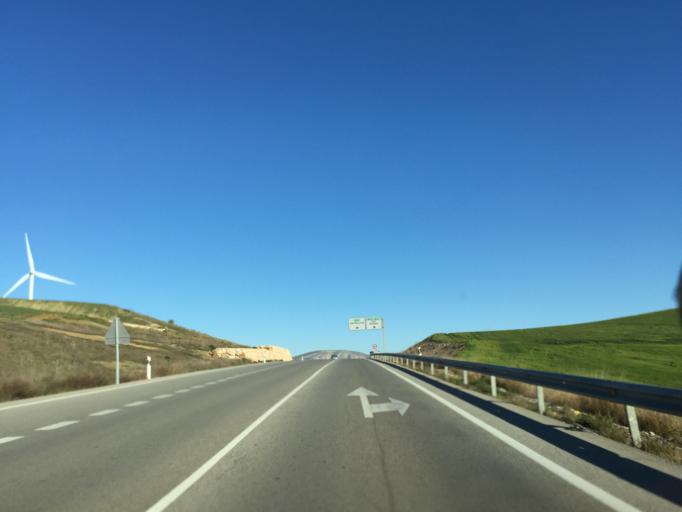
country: ES
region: Andalusia
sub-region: Provincia de Malaga
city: Ardales
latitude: 36.9354
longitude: -4.8630
